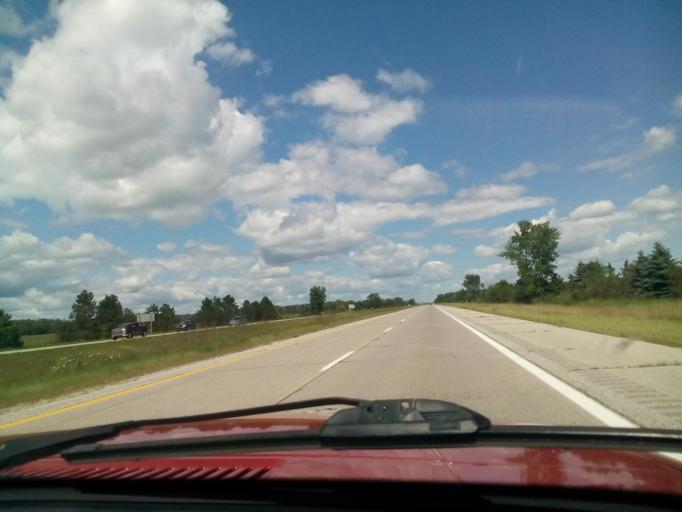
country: US
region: Michigan
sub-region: Bay County
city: Auburn
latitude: 43.6834
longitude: -84.0128
